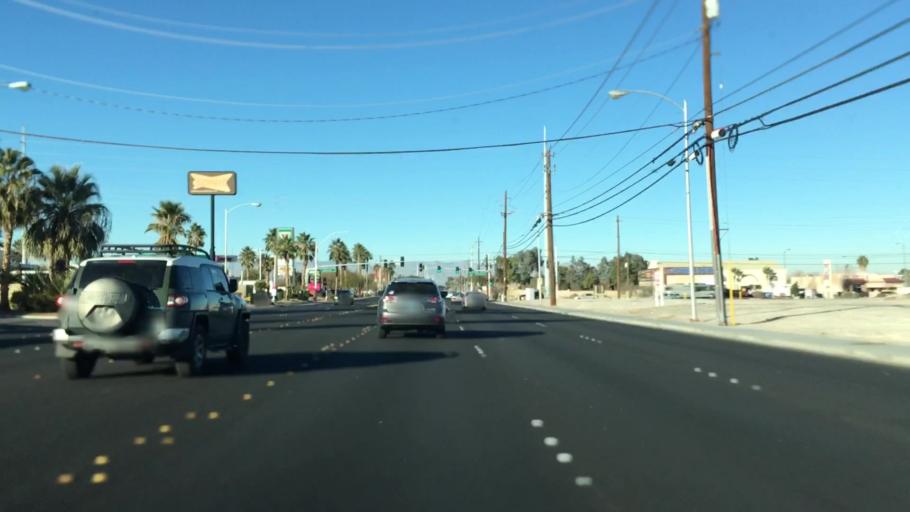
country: US
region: Nevada
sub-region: Clark County
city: Whitney
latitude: 36.0776
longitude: -115.1009
